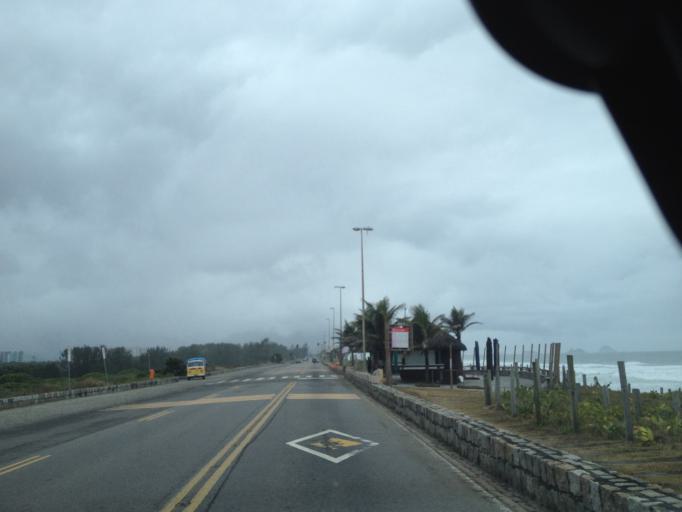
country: BR
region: Rio de Janeiro
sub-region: Nilopolis
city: Nilopolis
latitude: -23.0153
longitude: -43.4096
